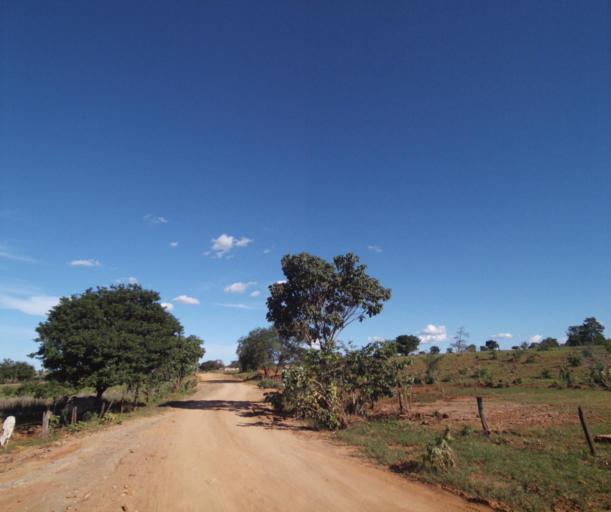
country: BR
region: Bahia
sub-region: Carinhanha
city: Carinhanha
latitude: -14.2773
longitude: -44.5021
